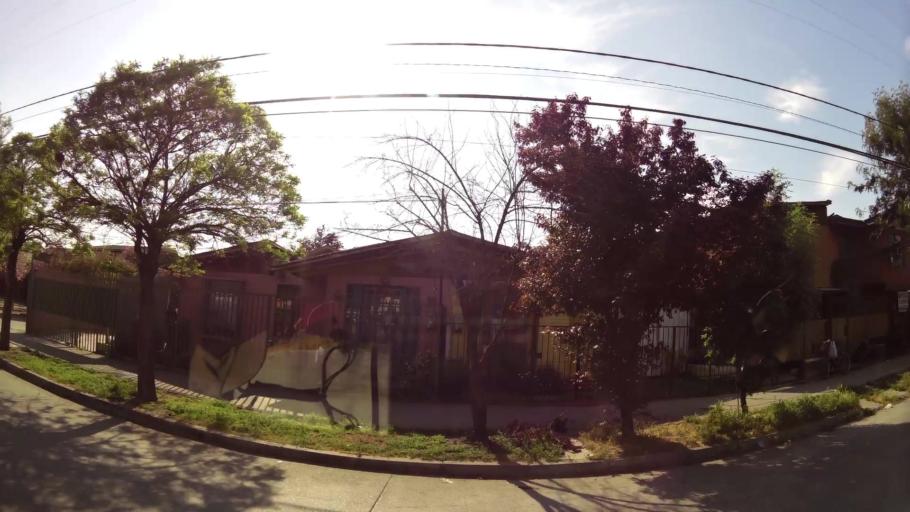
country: CL
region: Santiago Metropolitan
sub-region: Provincia de Santiago
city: La Pintana
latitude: -33.5549
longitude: -70.5985
